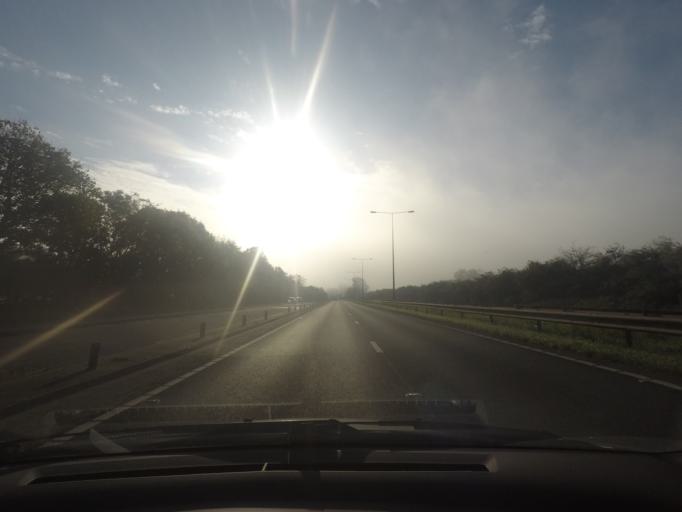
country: GB
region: England
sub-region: East Riding of Yorkshire
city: Welton
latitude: 53.7381
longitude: -0.5619
